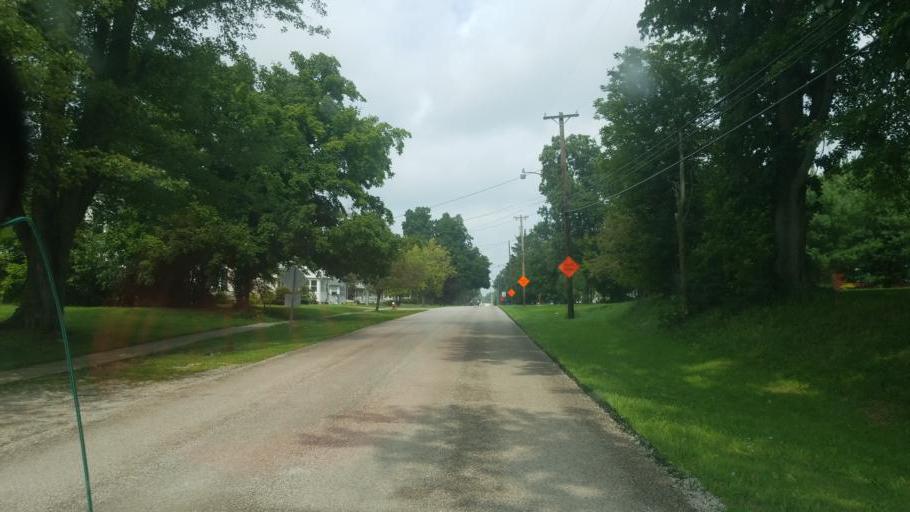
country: US
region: Ohio
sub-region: Huron County
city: Greenwich
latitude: 41.0356
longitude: -82.5164
